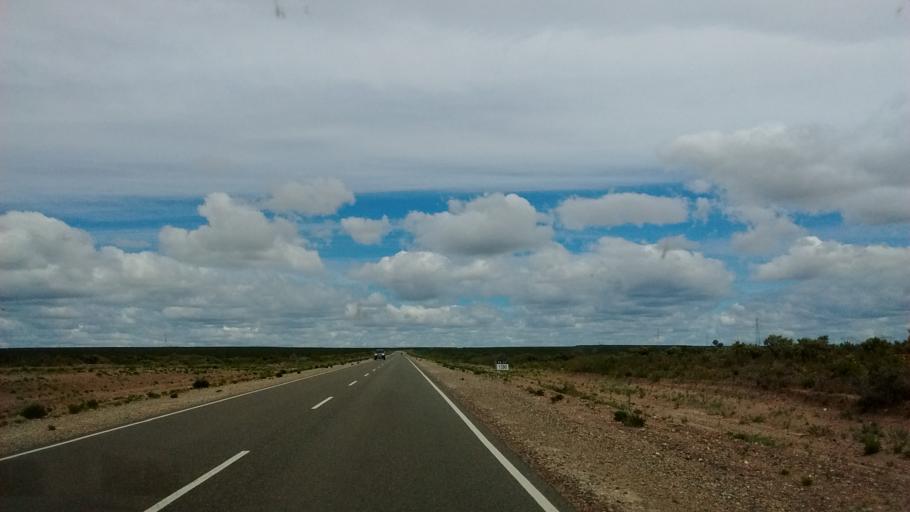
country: AR
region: Neuquen
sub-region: Departamento de Picun Leufu
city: Picun Leufu
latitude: -39.7424
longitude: -69.6051
